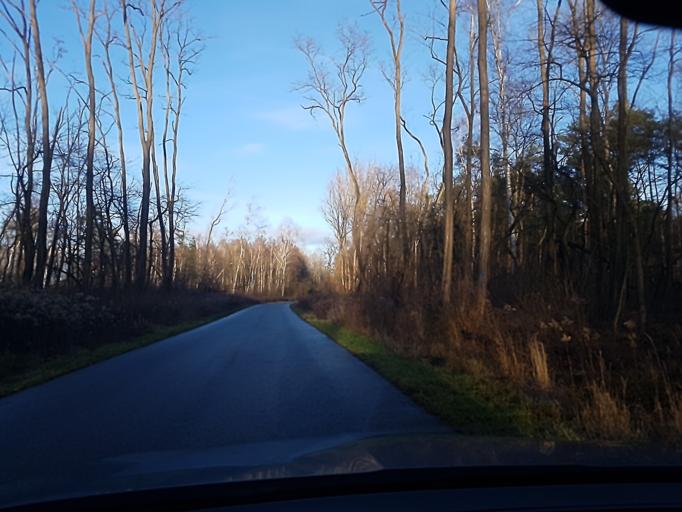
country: DE
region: Brandenburg
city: Trobitz
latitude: 51.5874
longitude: 13.4193
